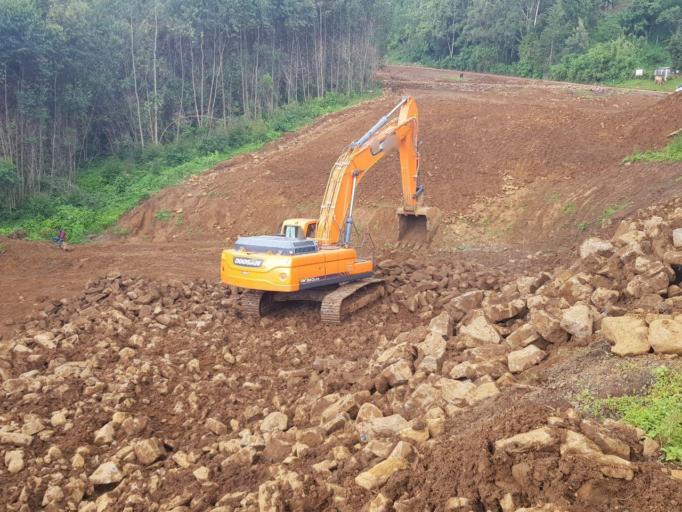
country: ET
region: Oromiya
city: Gore
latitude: 7.7009
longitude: 35.4907
